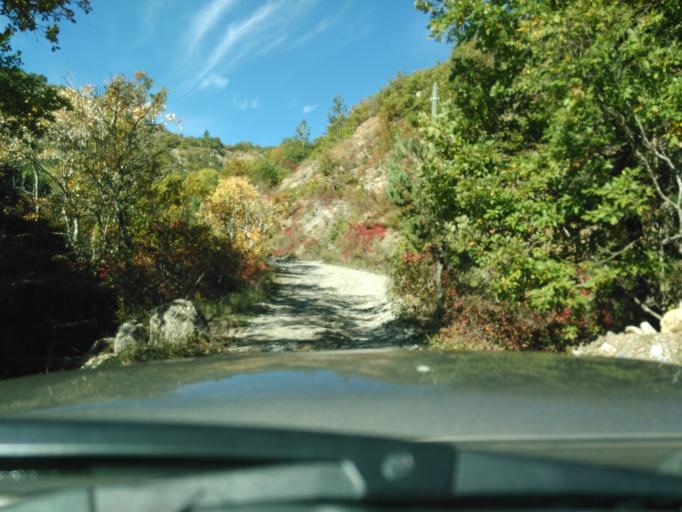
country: FR
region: Provence-Alpes-Cote d'Azur
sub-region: Departement des Alpes-de-Haute-Provence
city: Le Brusquet
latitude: 44.1879
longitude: 6.2642
